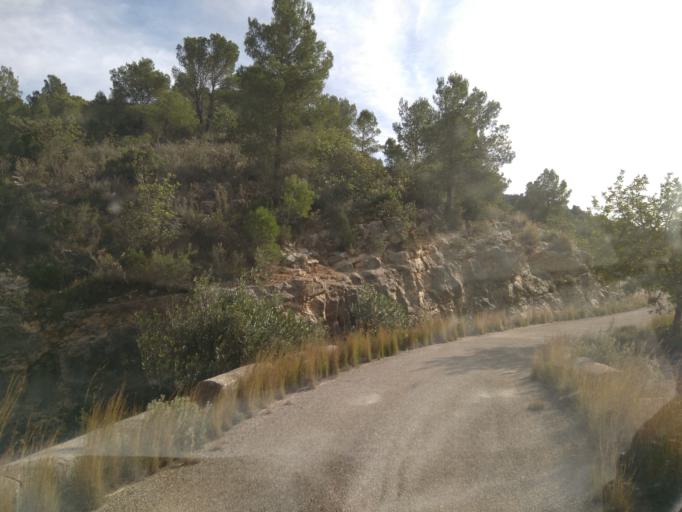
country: ES
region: Valencia
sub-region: Provincia de Valencia
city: Sumacarcer
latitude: 39.1552
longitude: -0.6510
